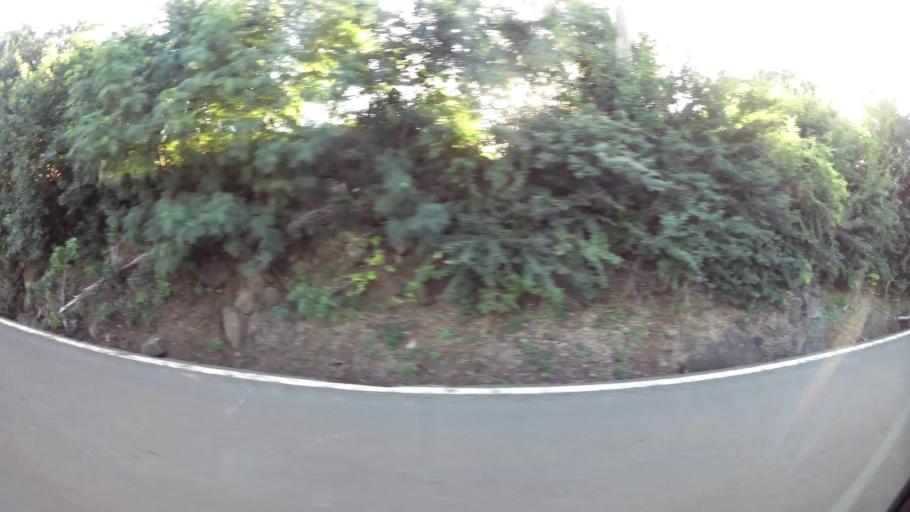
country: RE
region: Reunion
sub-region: Reunion
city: Saint-Louis
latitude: -21.2651
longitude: 55.3802
